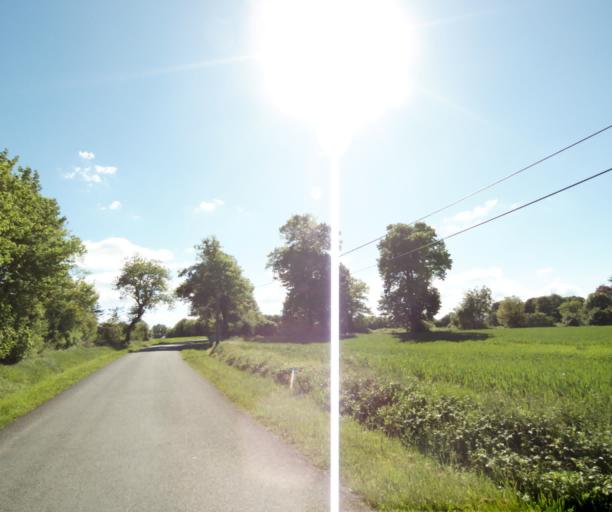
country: FR
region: Poitou-Charentes
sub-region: Departement de la Charente-Maritime
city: Saint-Georges-des-Coteaux
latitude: 45.7960
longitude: -0.6874
